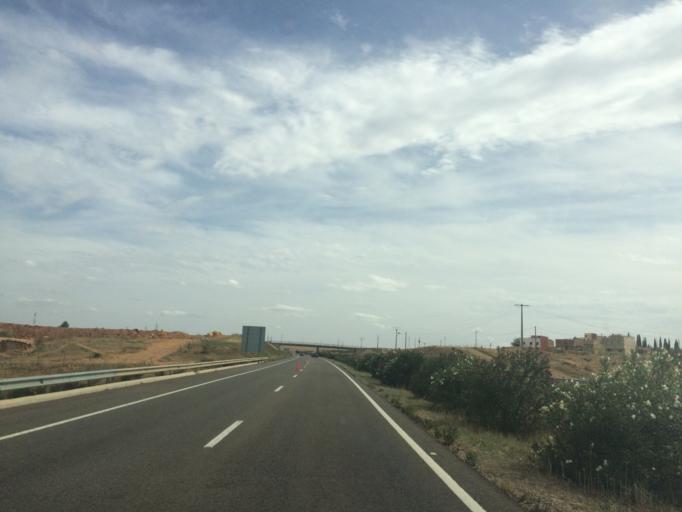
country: MA
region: Meknes-Tafilalet
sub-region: Meknes
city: Meknes
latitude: 33.8312
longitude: -5.5564
